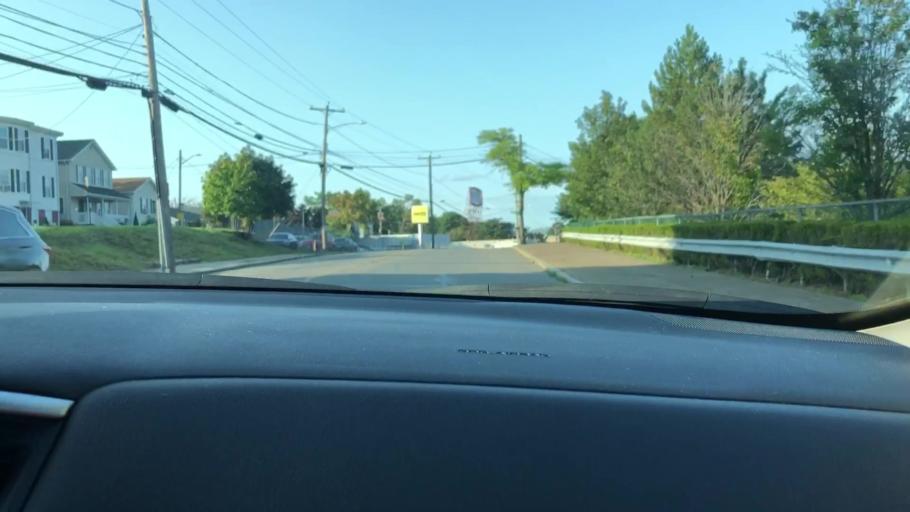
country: US
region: Rhode Island
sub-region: Providence County
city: Providence
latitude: 41.8534
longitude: -71.4126
